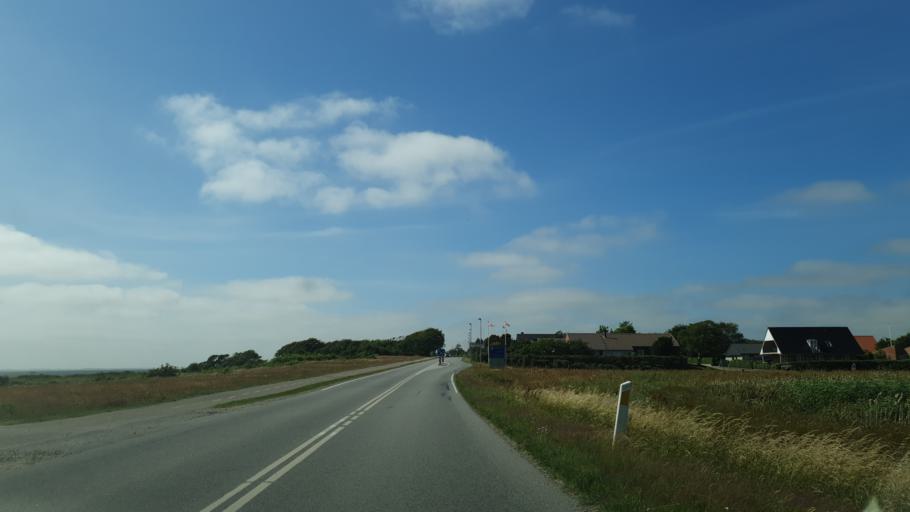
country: DK
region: Central Jutland
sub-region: Ringkobing-Skjern Kommune
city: Ringkobing
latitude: 56.0690
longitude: 8.2794
